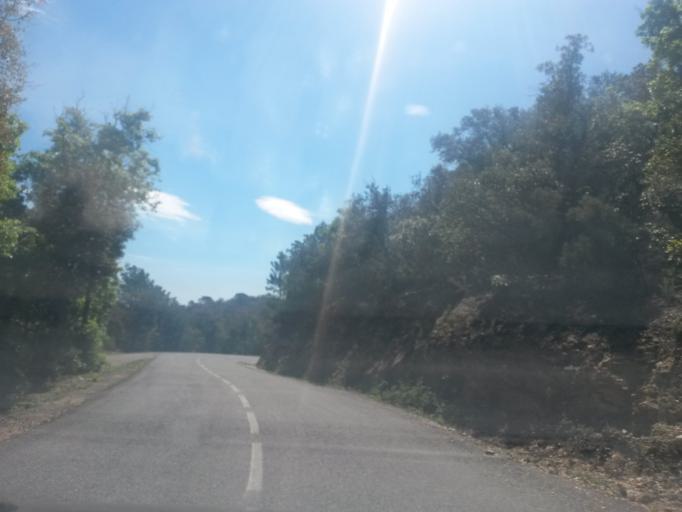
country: ES
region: Catalonia
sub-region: Provincia de Girona
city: Juia
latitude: 41.9831
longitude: 2.9233
